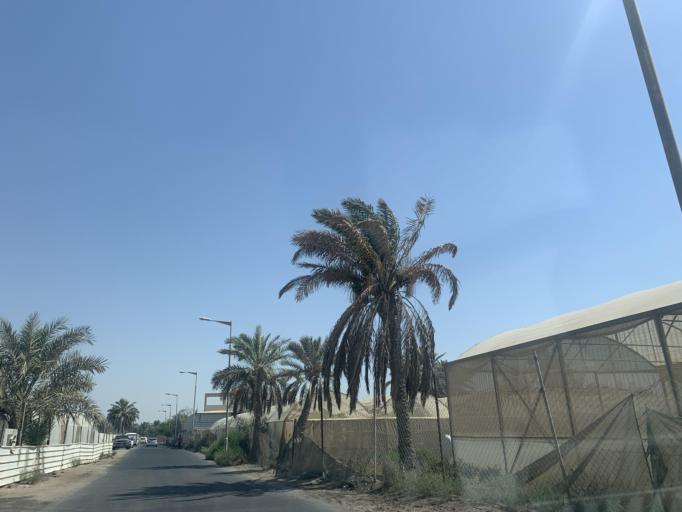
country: BH
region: Manama
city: Jidd Hafs
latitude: 26.2253
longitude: 50.5070
